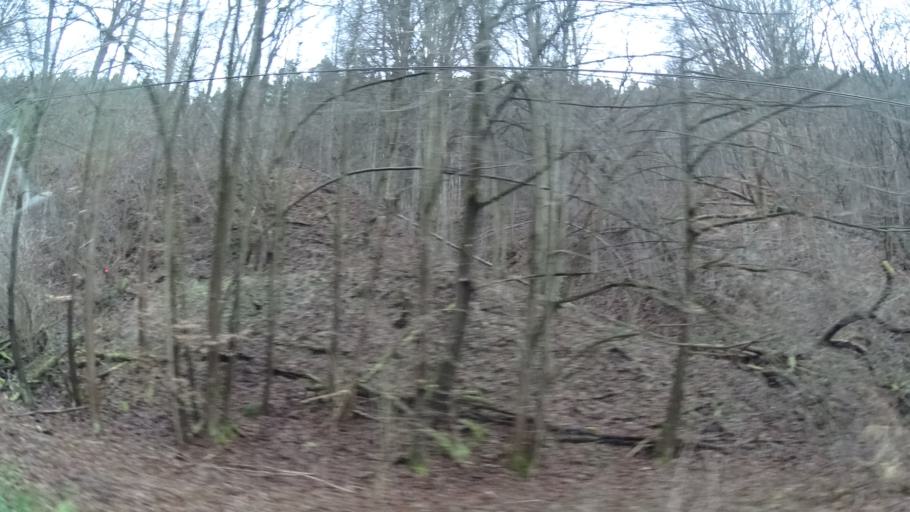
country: DE
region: Thuringia
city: Orlamunde
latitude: 50.7478
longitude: 11.4630
